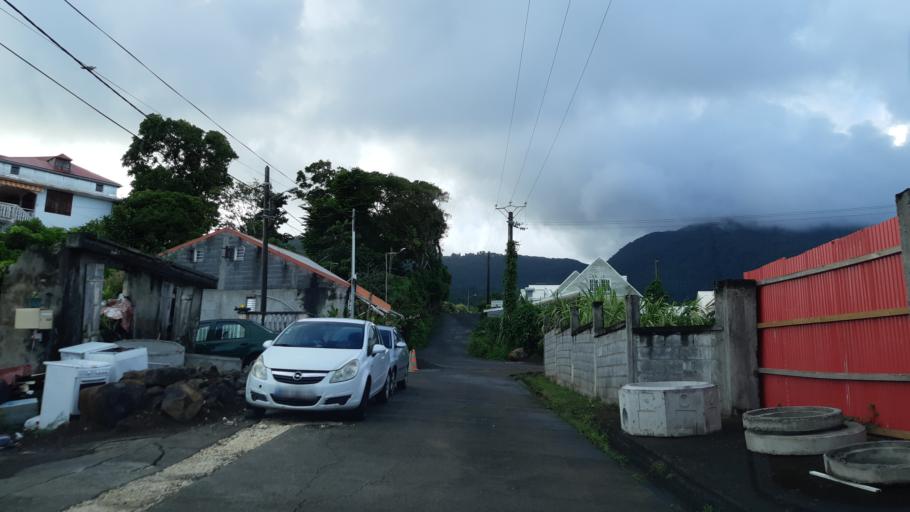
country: GP
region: Guadeloupe
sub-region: Guadeloupe
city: Trois-Rivieres
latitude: 15.9808
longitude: -61.6436
